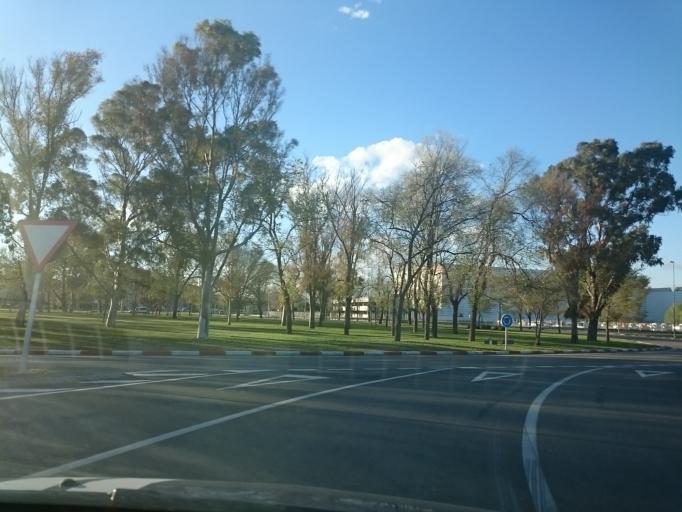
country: ES
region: Catalonia
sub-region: Provincia de Barcelona
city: El Prat de Llobregat
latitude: 41.3237
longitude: 2.1078
